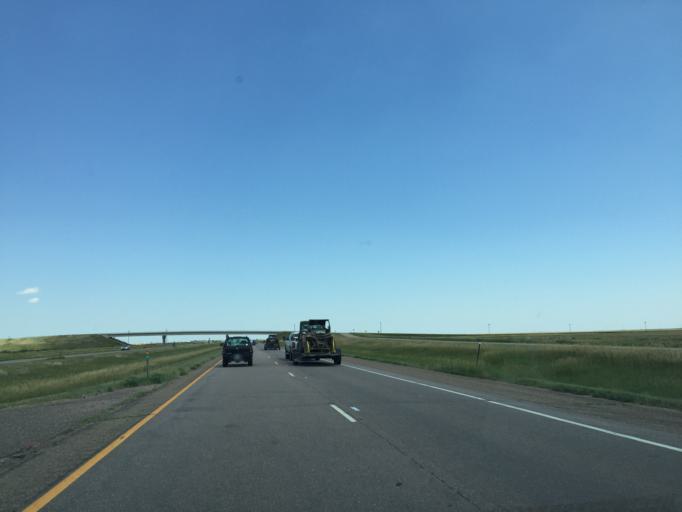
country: US
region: Colorado
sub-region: Lincoln County
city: Hugo
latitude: 39.2808
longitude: -103.3477
